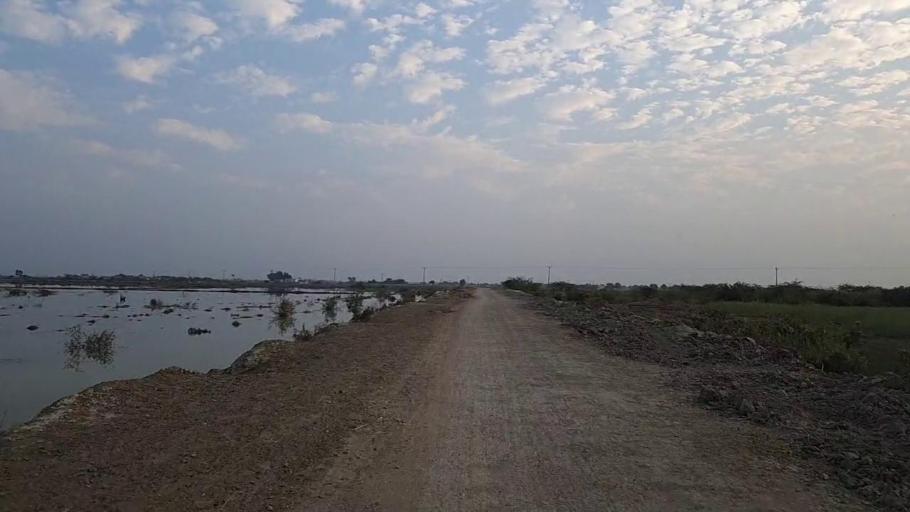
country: PK
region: Sindh
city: Pithoro
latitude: 25.4429
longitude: 69.3450
